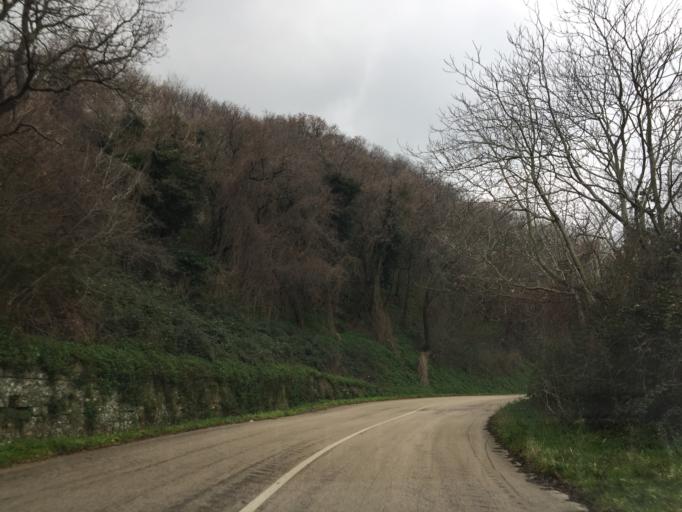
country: IT
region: Apulia
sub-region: Provincia di Foggia
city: Bovino
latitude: 41.2614
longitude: 15.3629
